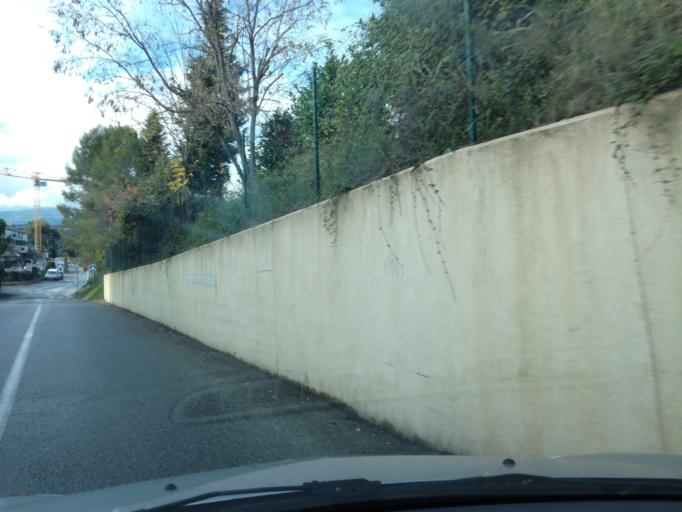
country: FR
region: Provence-Alpes-Cote d'Azur
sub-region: Departement des Alpes-Maritimes
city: Mouans-Sartoux
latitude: 43.6120
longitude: 6.9666
